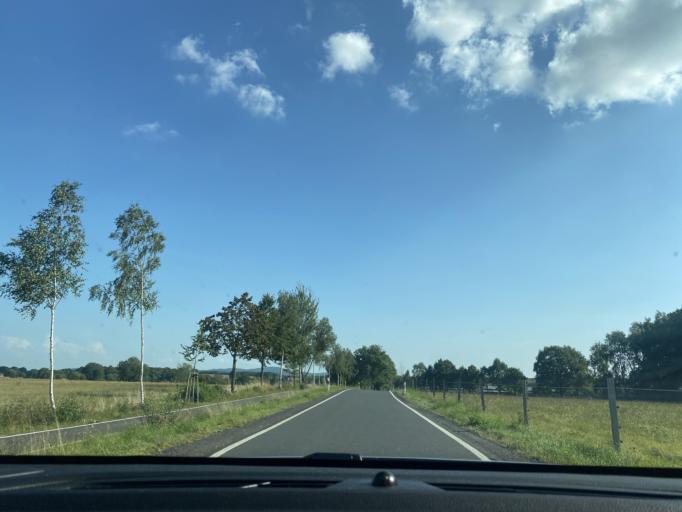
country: DE
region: Saxony
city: Quitzdorf
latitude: 51.2507
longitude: 14.7575
